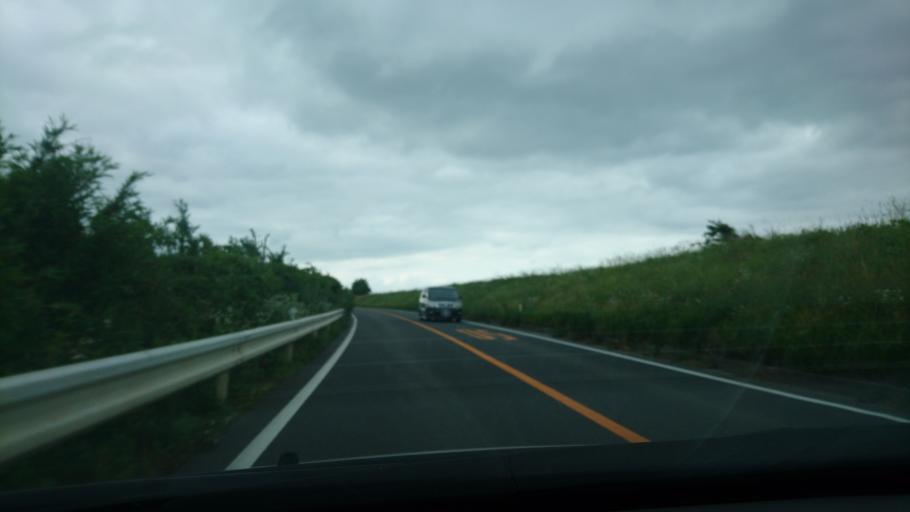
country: JP
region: Iwate
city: Ichinoseki
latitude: 38.7393
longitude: 141.1520
